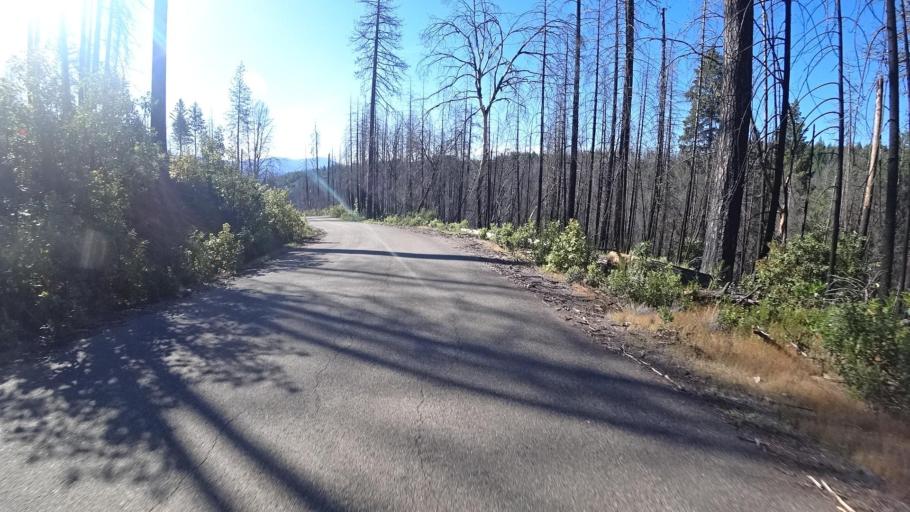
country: US
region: California
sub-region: Lake County
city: Upper Lake
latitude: 39.3973
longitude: -122.9646
